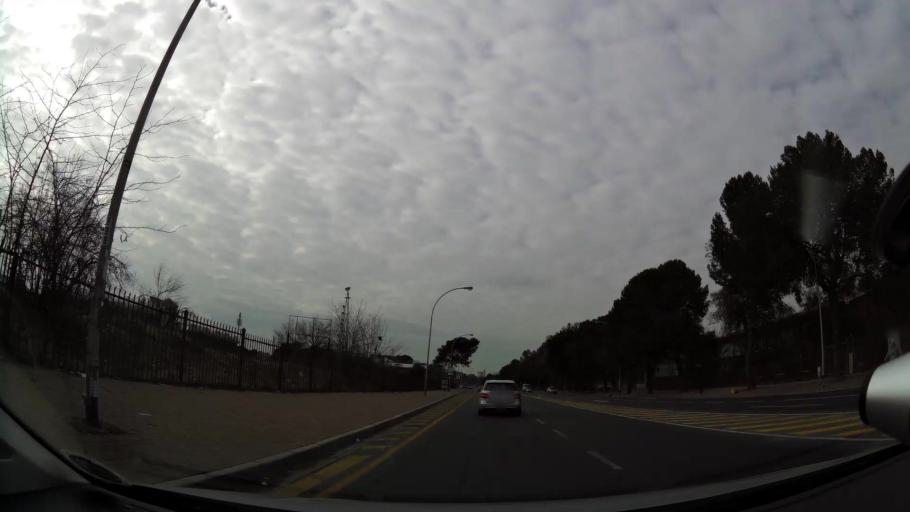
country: ZA
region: Orange Free State
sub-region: Mangaung Metropolitan Municipality
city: Bloemfontein
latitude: -29.1195
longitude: 26.2047
